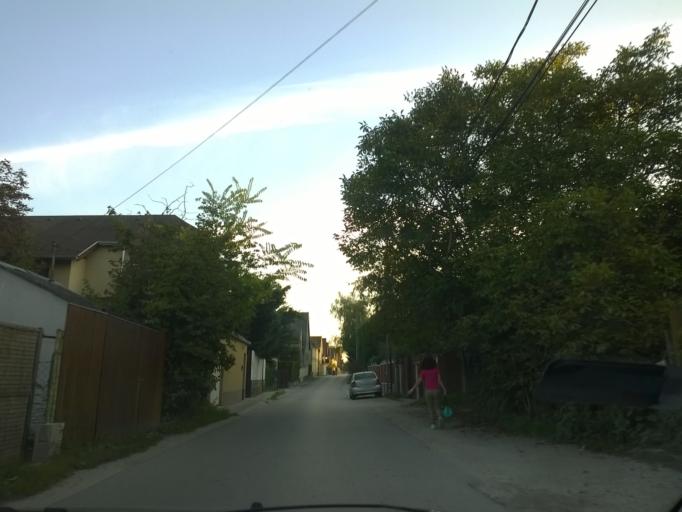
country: HU
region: Pest
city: Szigetszentmiklos
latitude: 47.3333
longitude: 19.0462
